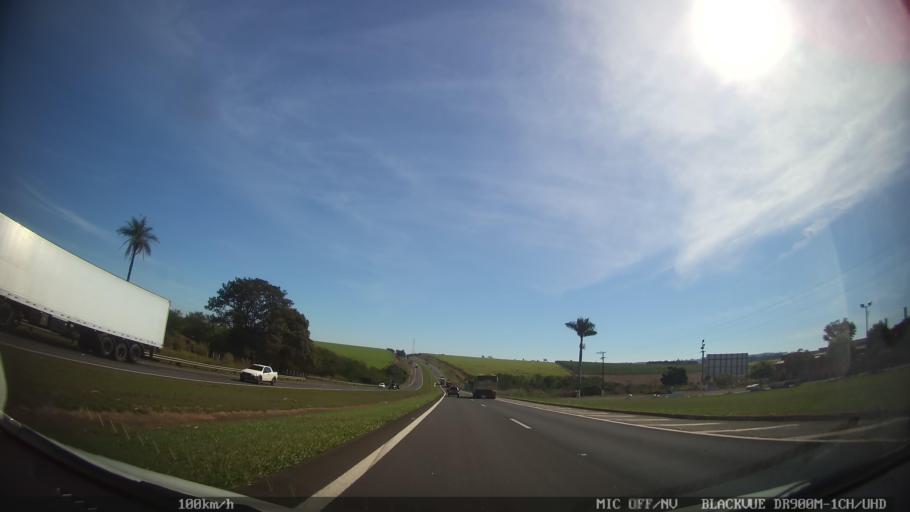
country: BR
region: Sao Paulo
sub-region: Porto Ferreira
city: Porto Ferreira
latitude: -21.8057
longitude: -47.5026
